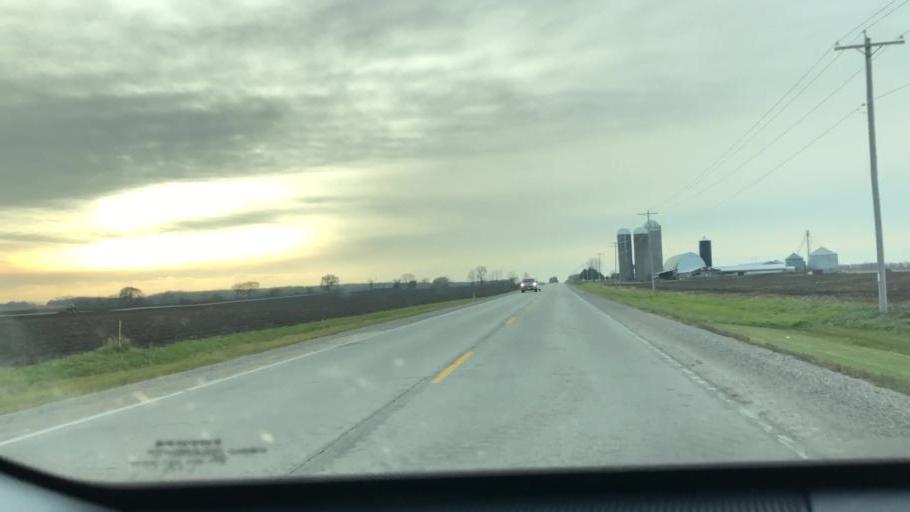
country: US
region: Wisconsin
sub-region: Outagamie County
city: Seymour
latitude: 44.4438
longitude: -88.2978
